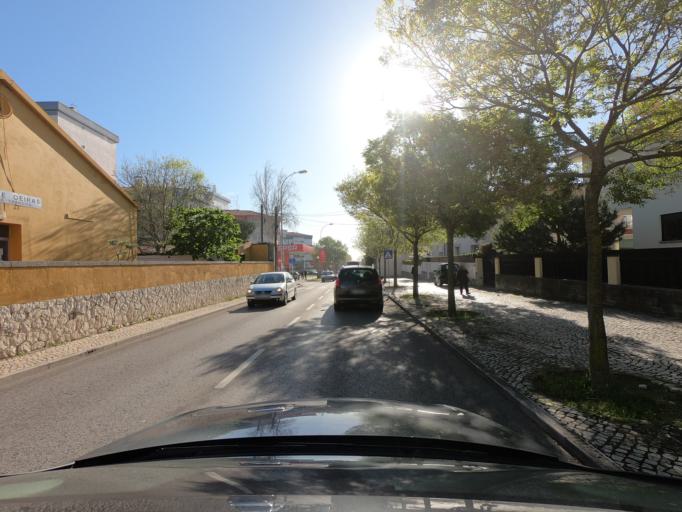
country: PT
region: Lisbon
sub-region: Oeiras
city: Oeiras
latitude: 38.6934
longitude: -9.3074
